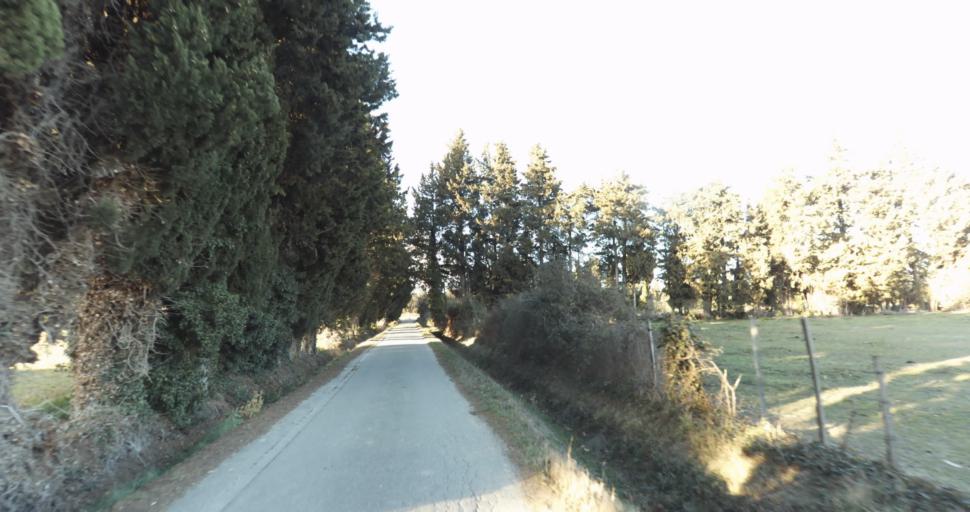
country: FR
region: Provence-Alpes-Cote d'Azur
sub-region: Departement des Bouches-du-Rhone
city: Barbentane
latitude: 43.9135
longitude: 4.7562
